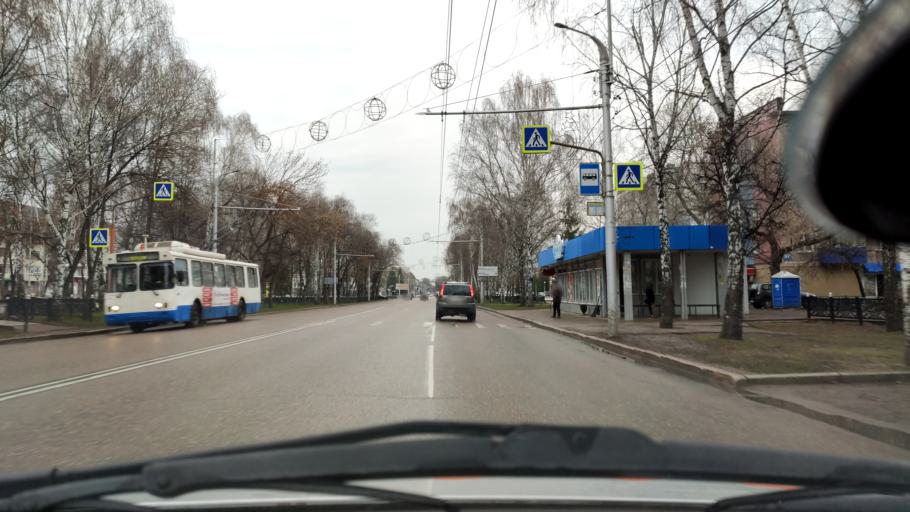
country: RU
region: Bashkortostan
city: Sterlitamak
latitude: 53.6345
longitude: 55.9346
